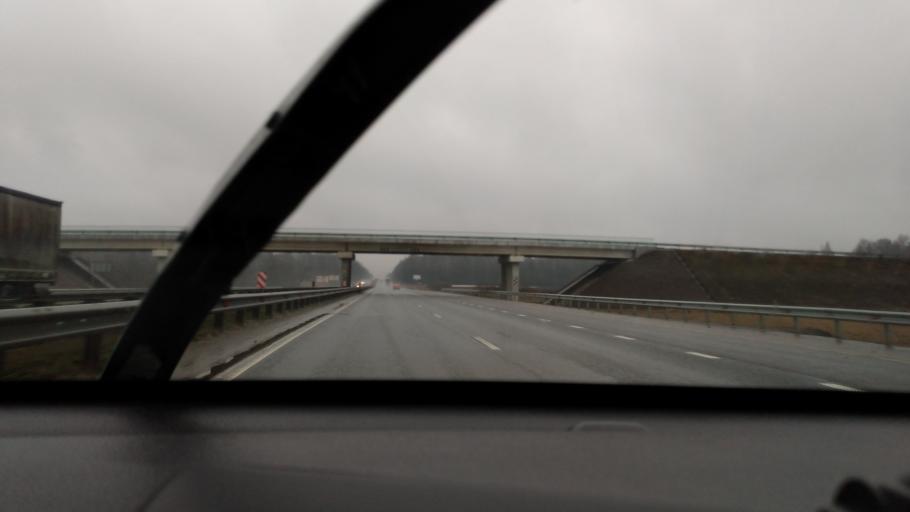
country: RU
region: Tula
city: Venev
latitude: 54.3760
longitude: 38.1549
